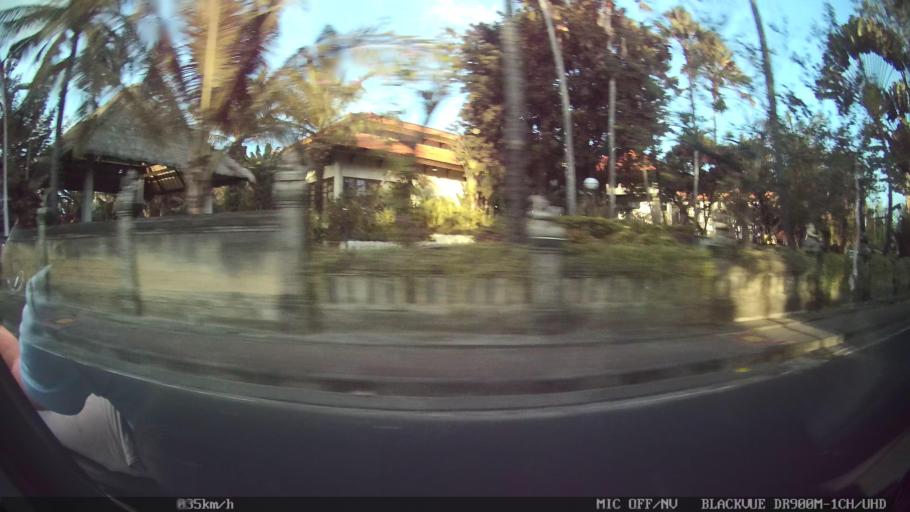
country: ID
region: Bali
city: Bualu
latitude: -8.7676
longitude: 115.2218
